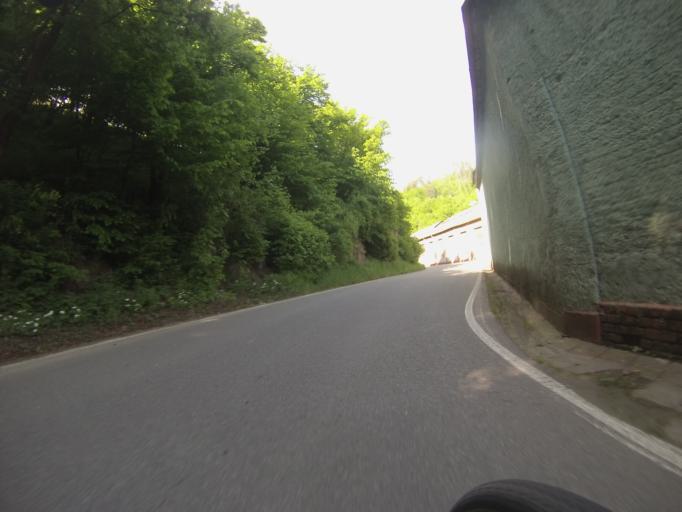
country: CZ
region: South Moravian
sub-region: Okres Blansko
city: Blansko
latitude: 49.3542
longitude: 16.6849
